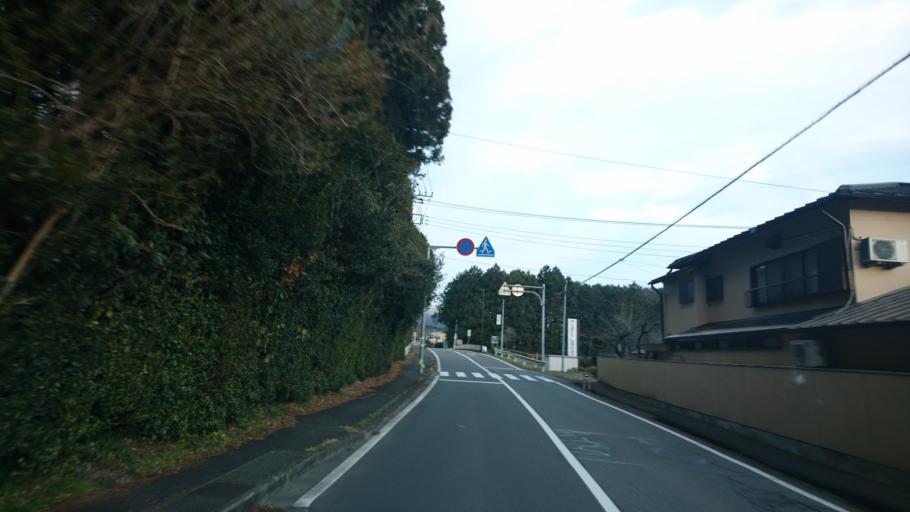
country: JP
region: Shizuoka
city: Fujinomiya
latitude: 35.3117
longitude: 138.5972
